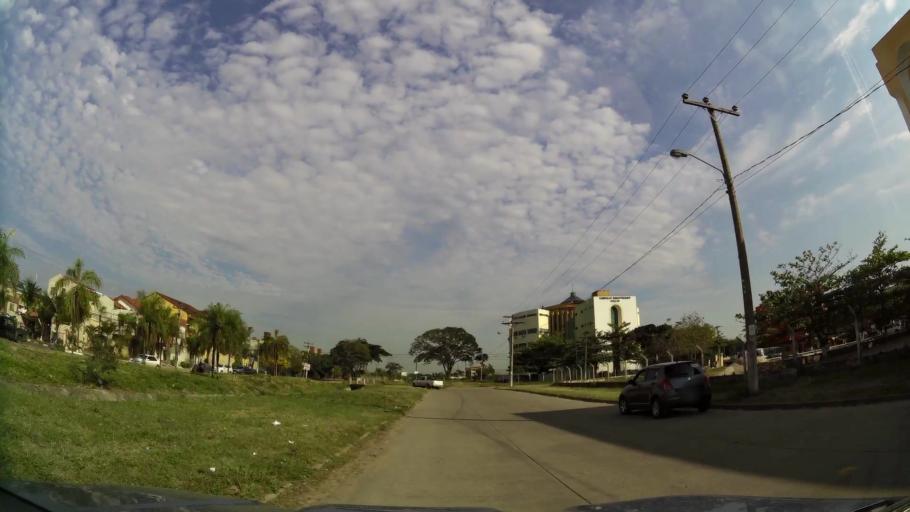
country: BO
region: Santa Cruz
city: Santa Cruz de la Sierra
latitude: -17.7309
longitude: -63.1716
